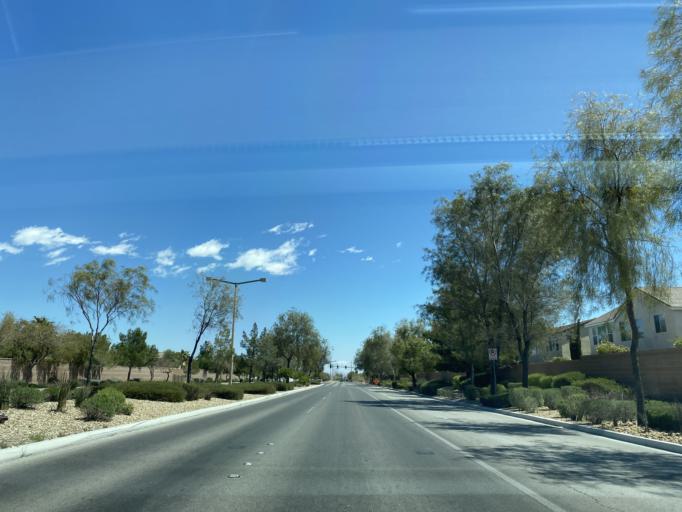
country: US
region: Nevada
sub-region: Clark County
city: North Las Vegas
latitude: 36.3053
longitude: -115.2180
